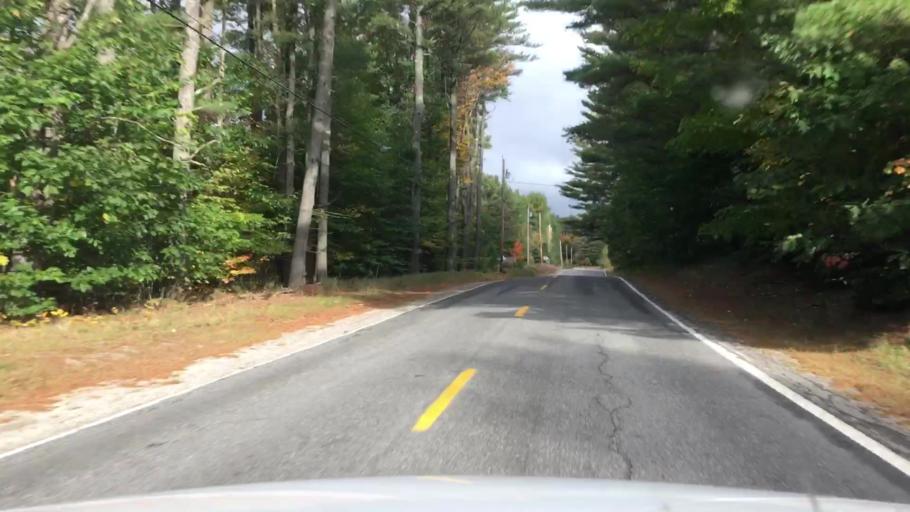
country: US
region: Maine
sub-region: Oxford County
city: Bethel
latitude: 44.3355
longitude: -70.7786
